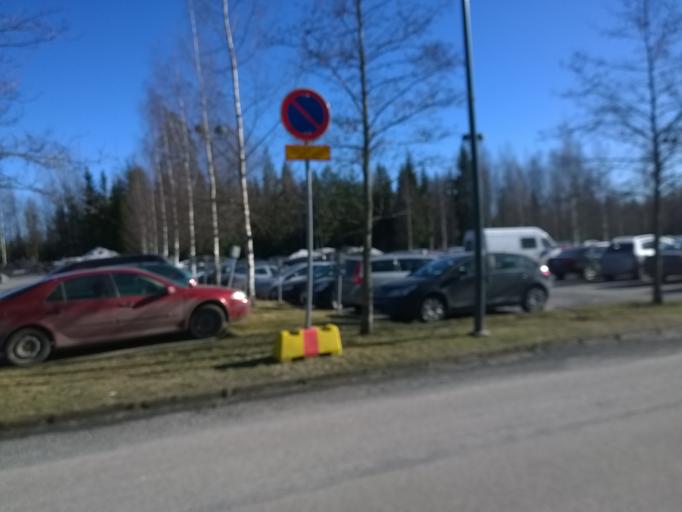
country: FI
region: Pirkanmaa
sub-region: Tampere
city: Tampere
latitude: 61.4484
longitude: 23.8644
